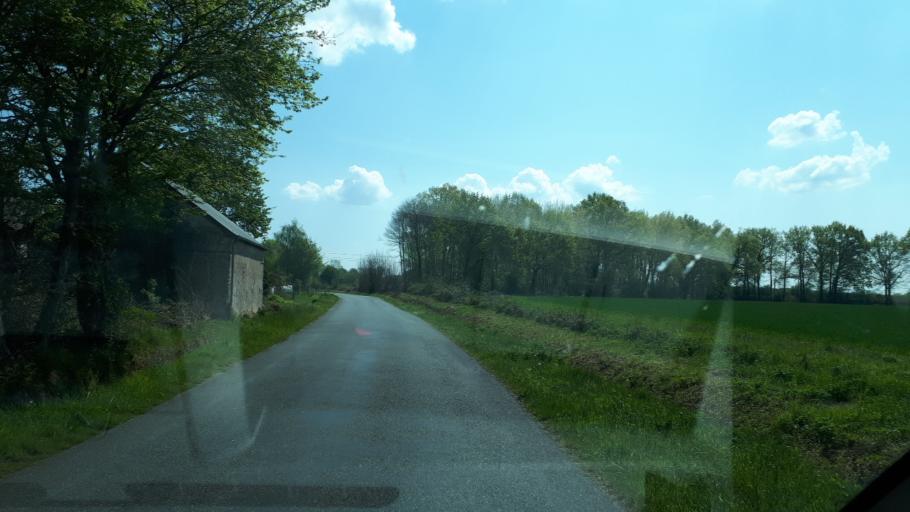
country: FR
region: Centre
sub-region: Departement du Cher
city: Neuvy-sur-Barangeon
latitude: 47.3190
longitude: 2.3425
